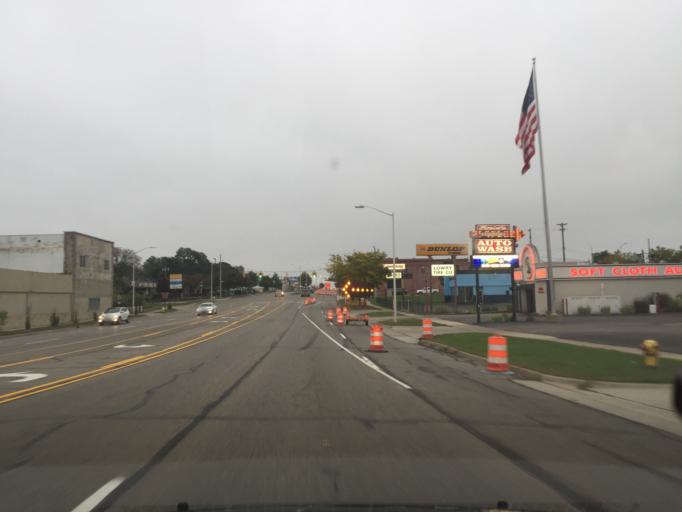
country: US
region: Michigan
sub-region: Oakland County
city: Pontiac
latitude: 42.6282
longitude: -83.2876
